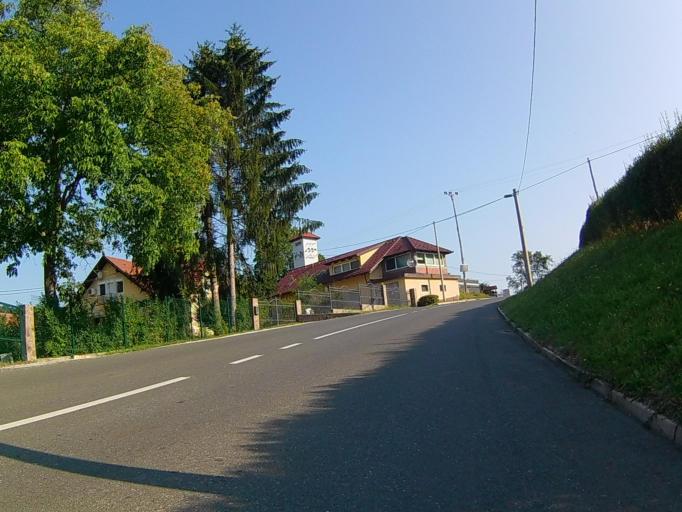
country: SI
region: Maribor
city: Kamnica
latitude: 46.6009
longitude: 15.6211
